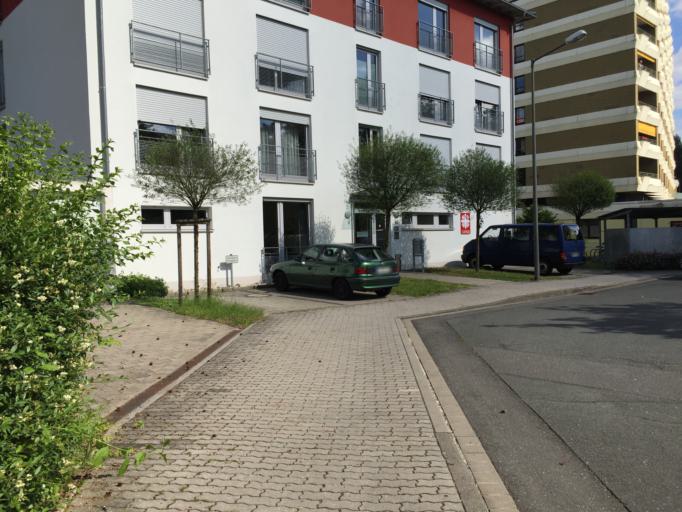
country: DE
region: Bavaria
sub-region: Regierungsbezirk Mittelfranken
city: Erlangen
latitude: 49.5730
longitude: 11.0159
